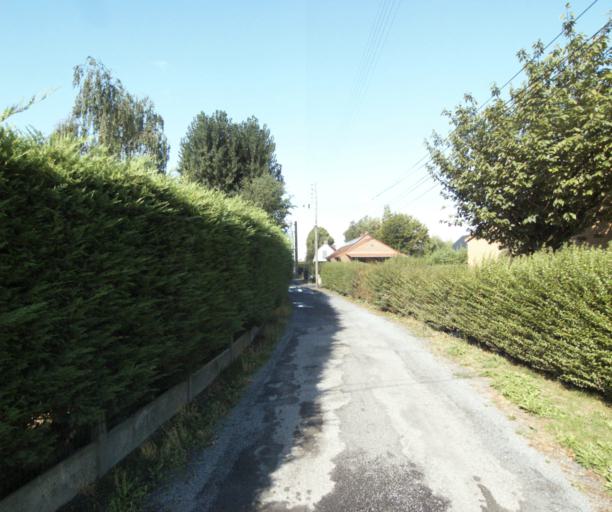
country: FR
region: Nord-Pas-de-Calais
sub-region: Departement du Nord
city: Sailly-lez-Lannoy
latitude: 50.6555
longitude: 3.2206
